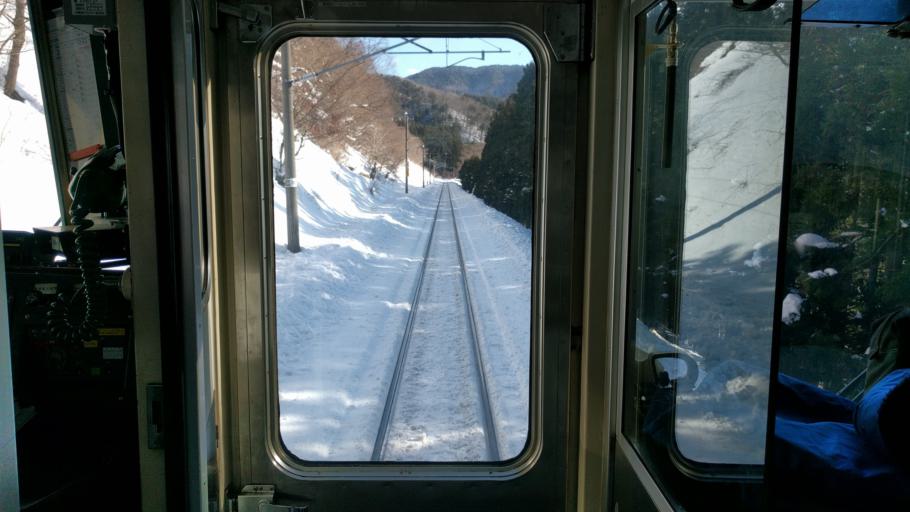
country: JP
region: Fukushima
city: Inawashiro
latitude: 37.4950
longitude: 140.2083
